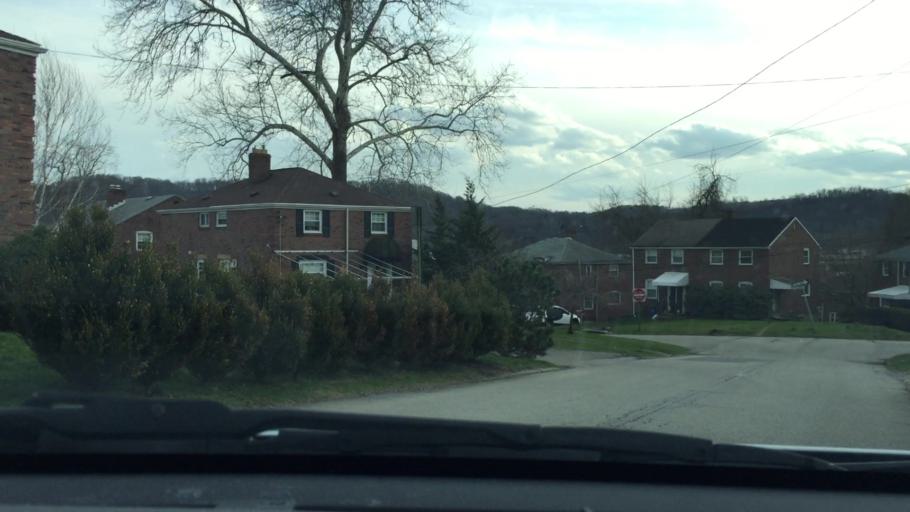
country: US
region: Pennsylvania
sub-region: Allegheny County
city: Leetsdale
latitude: 40.5627
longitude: -80.2043
